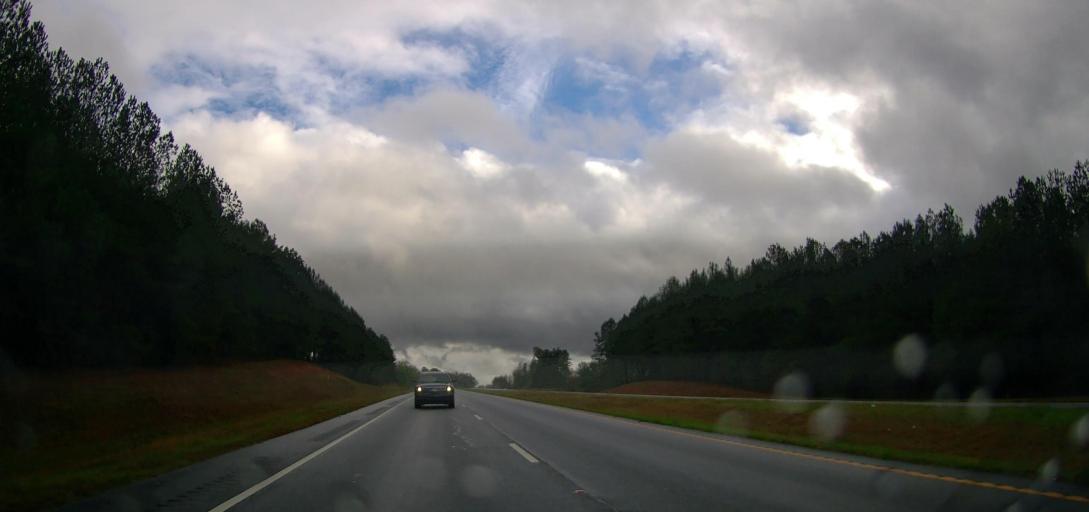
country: US
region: Georgia
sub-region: Jackson County
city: Nicholson
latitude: 34.0893
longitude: -83.4265
